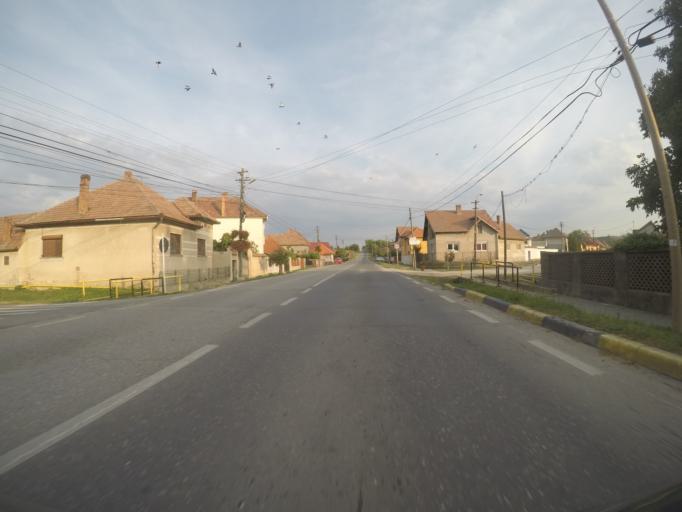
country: RO
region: Alba
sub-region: Municipiul Sebes
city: Sebes
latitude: 45.9522
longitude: 23.5812
